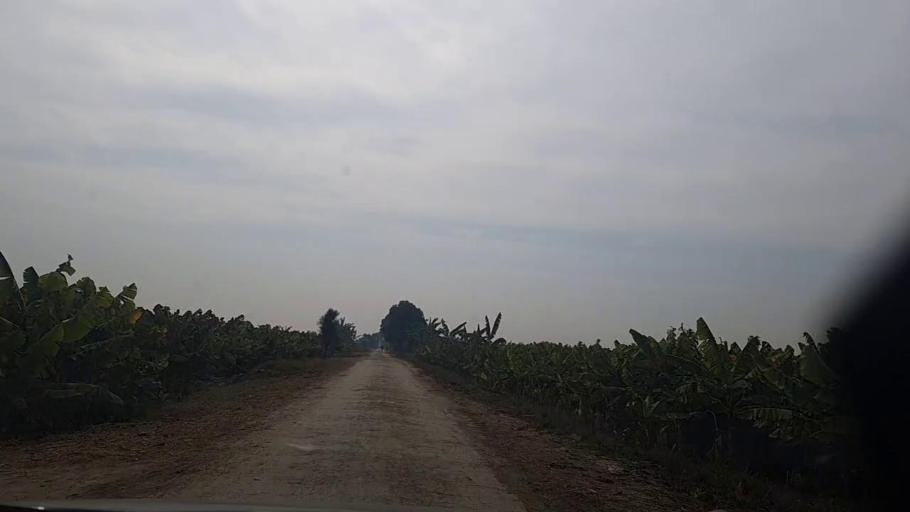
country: PK
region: Sindh
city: Sakrand
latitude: 26.2351
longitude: 68.2971
